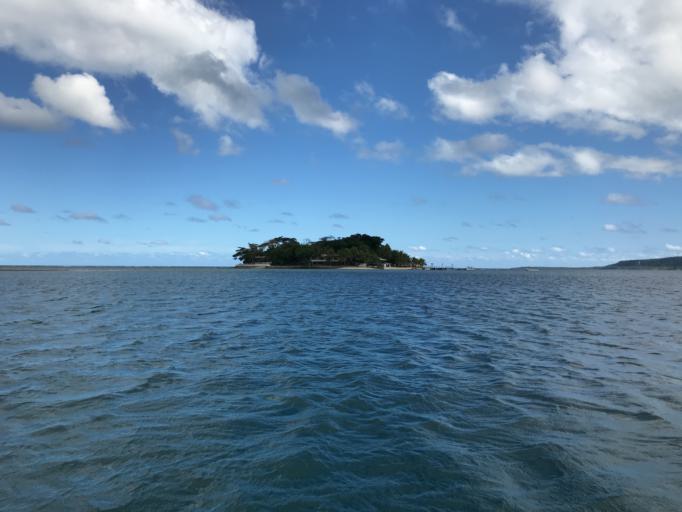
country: VU
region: Shefa
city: Port-Vila
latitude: -17.6940
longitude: 168.2658
